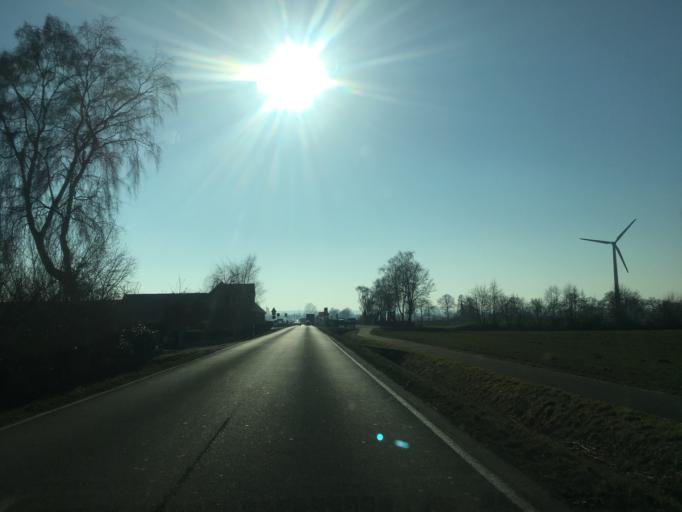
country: DE
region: North Rhine-Westphalia
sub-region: Regierungsbezirk Munster
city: Altenberge
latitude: 52.0191
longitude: 7.4437
